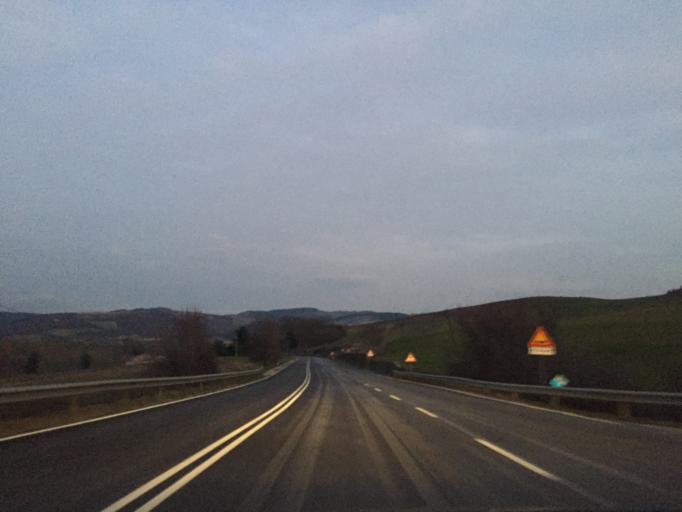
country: IT
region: Apulia
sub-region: Provincia di Foggia
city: Volturara Appula
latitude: 41.4568
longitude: 15.0643
